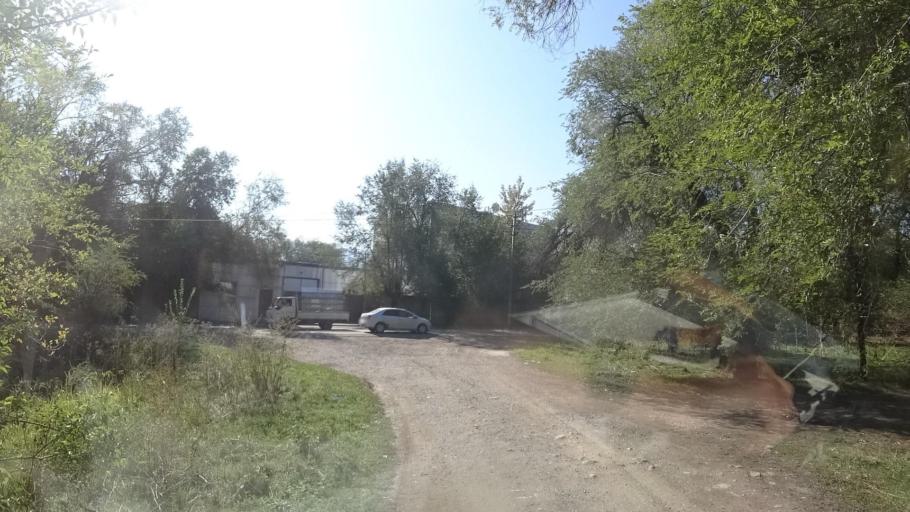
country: KZ
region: Almaty Oblysy
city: Pervomayskiy
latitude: 43.3303
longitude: 76.9999
